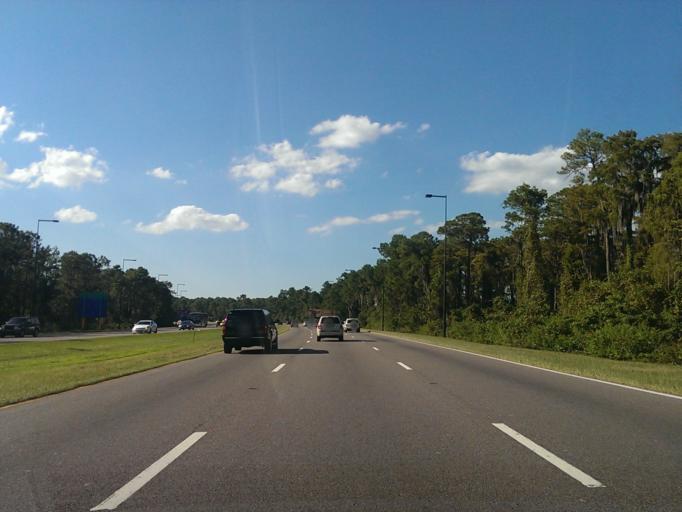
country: US
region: Florida
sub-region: Osceola County
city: Celebration
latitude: 28.3802
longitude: -81.5417
